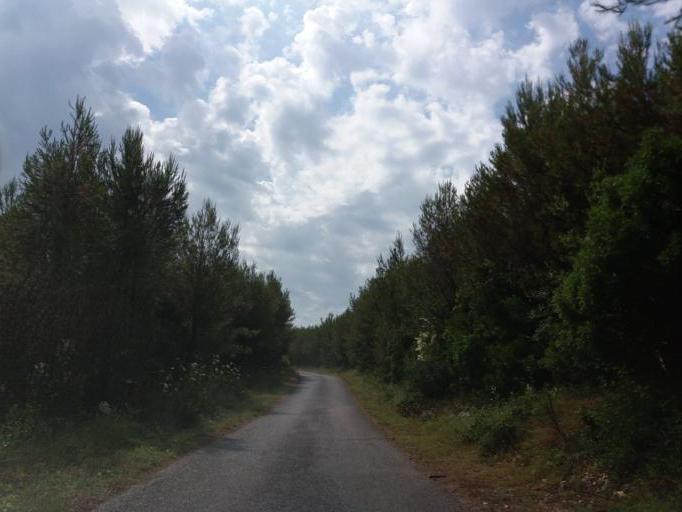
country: HR
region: Zadarska
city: Sali
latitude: 43.9118
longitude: 15.1272
